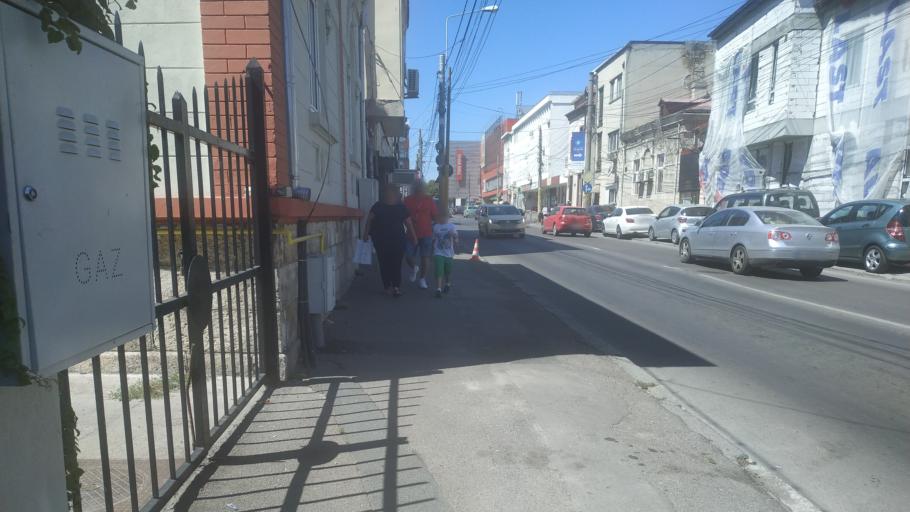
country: RO
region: Constanta
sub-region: Municipiul Constanta
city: Constanta
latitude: 44.1770
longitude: 28.6478
